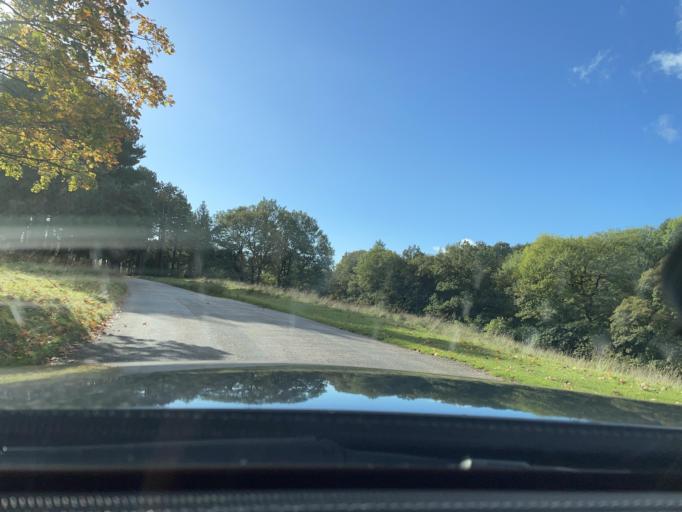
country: GB
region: England
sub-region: Cheshire East
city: Disley
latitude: 53.3520
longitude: -2.0546
